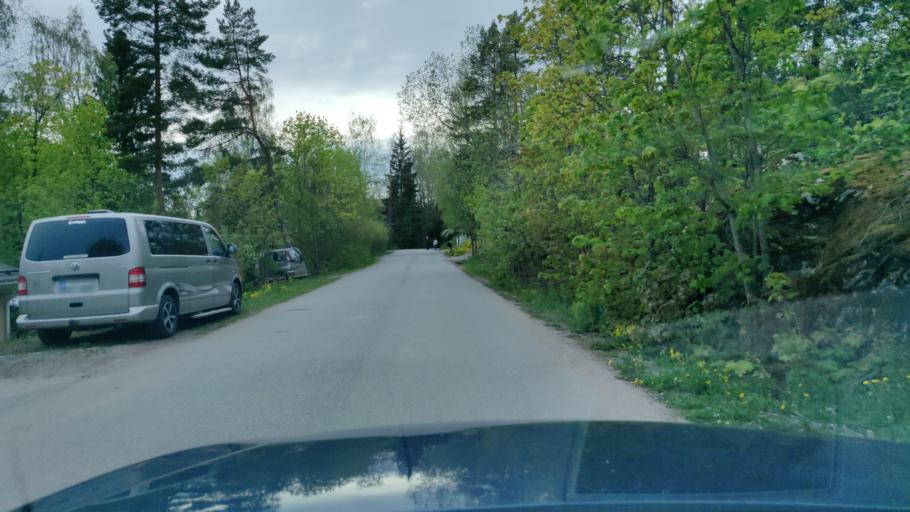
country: FI
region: Uusimaa
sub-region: Helsinki
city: Nurmijaervi
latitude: 60.3846
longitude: 24.7534
